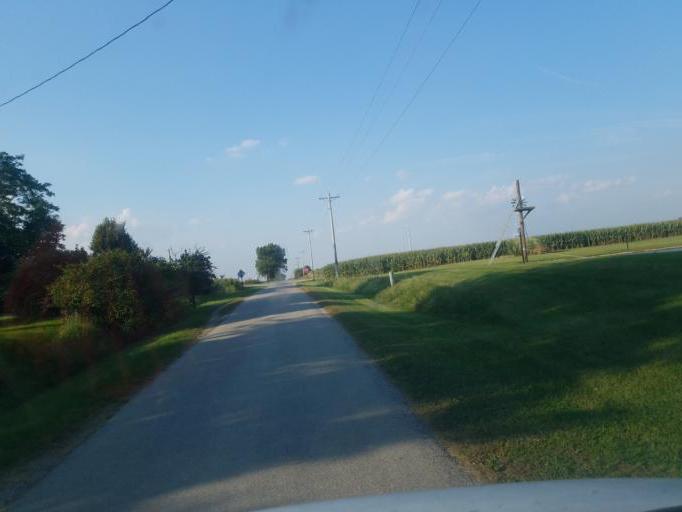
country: US
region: Ohio
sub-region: Seneca County
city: Tiffin
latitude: 40.9489
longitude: -83.1125
